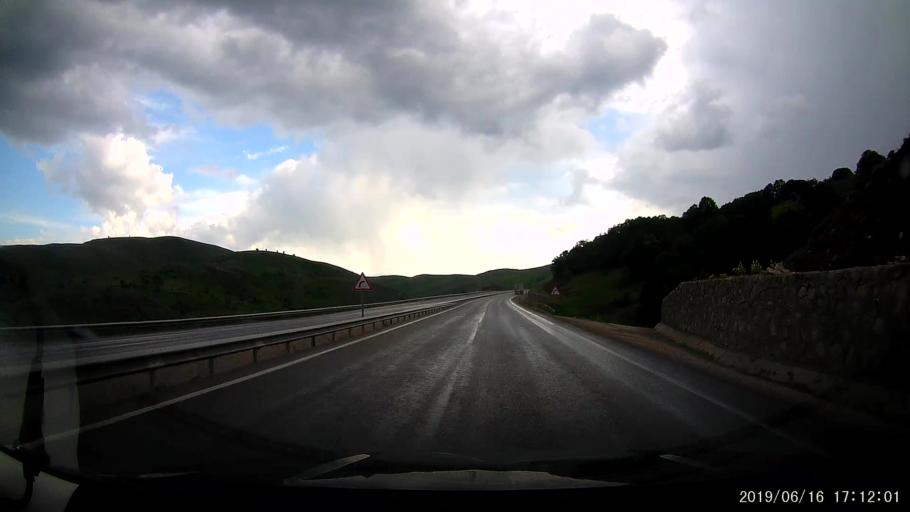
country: TR
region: Erzurum
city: Askale
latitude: 39.8597
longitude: 40.6230
